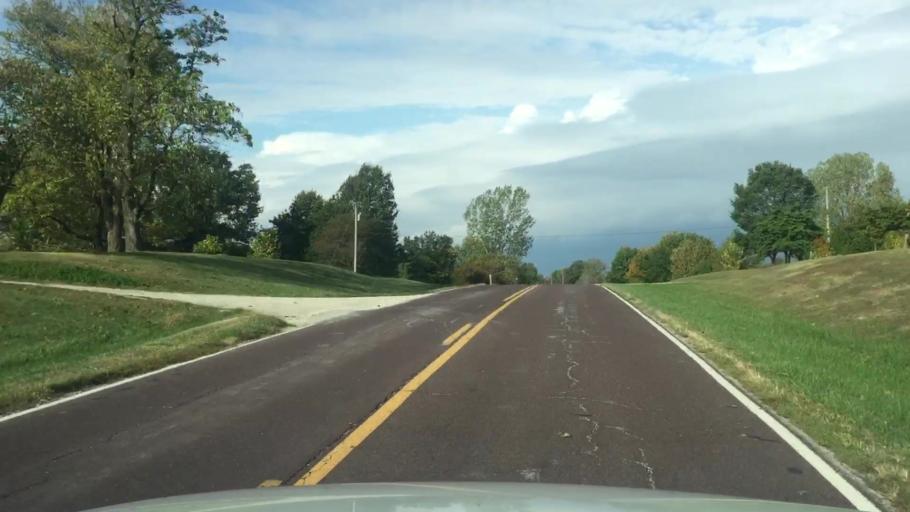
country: US
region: Missouri
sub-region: Boone County
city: Columbia
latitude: 38.8691
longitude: -92.2837
